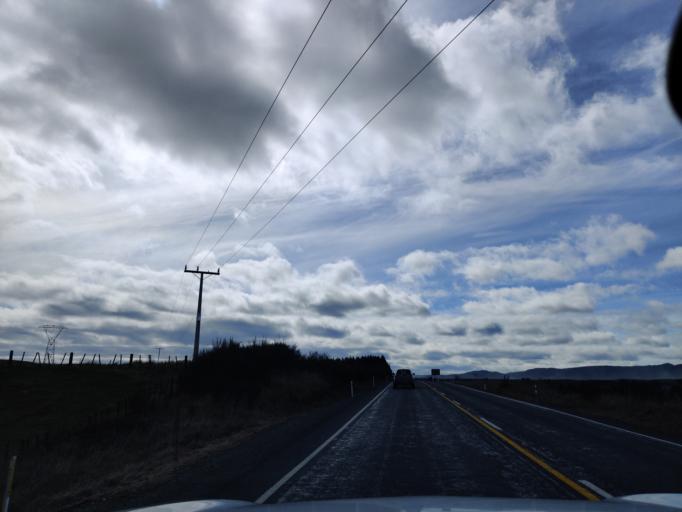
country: NZ
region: Waikato
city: Turangi
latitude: -39.0713
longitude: 175.8133
